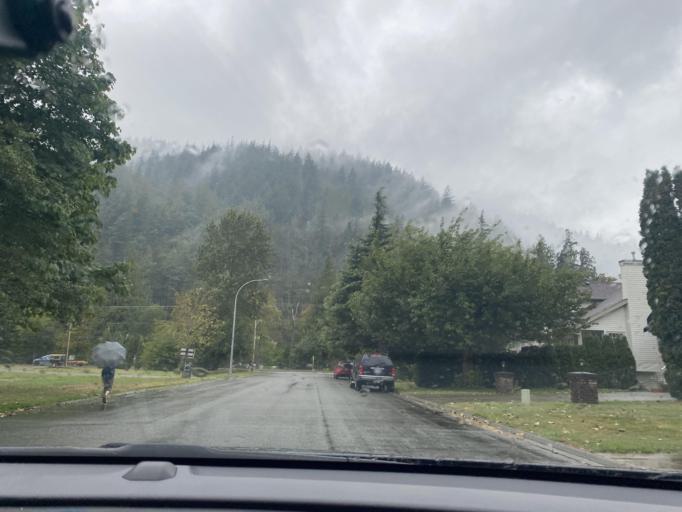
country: CA
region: British Columbia
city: Agassiz
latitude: 49.3005
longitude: -121.7839
